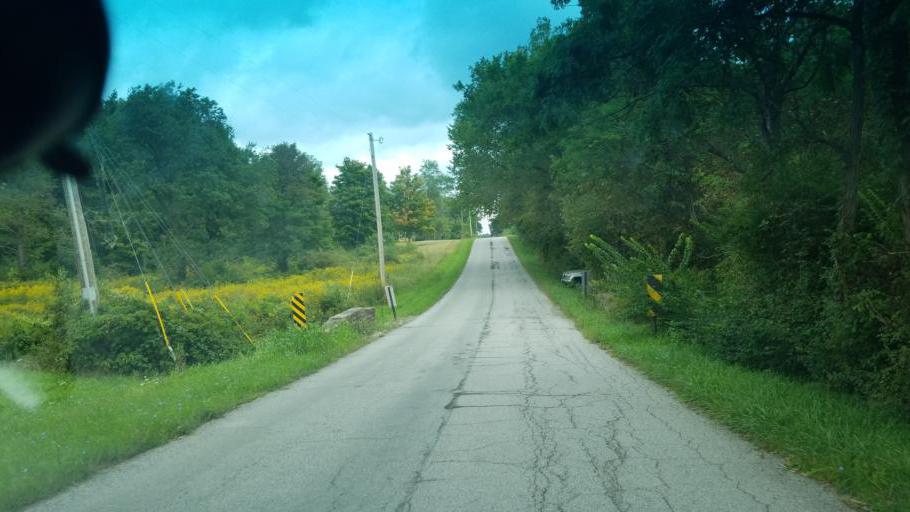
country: US
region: Ohio
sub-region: Richland County
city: Ontario
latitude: 40.8009
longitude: -82.5708
